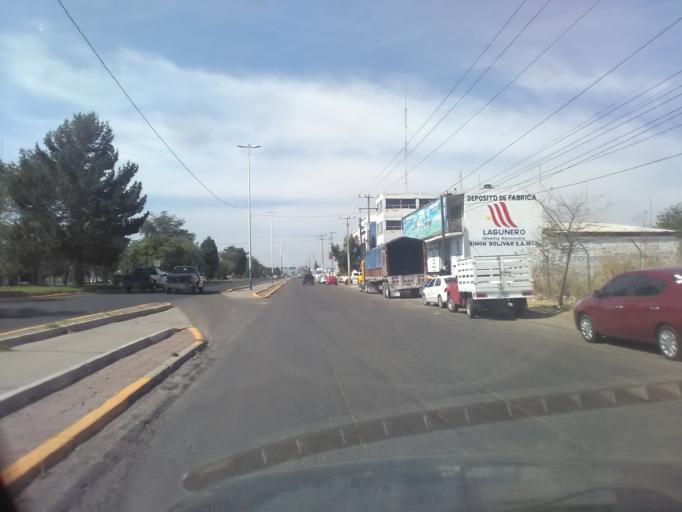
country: MX
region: Durango
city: Victoria de Durango
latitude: 24.0524
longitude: -104.6180
